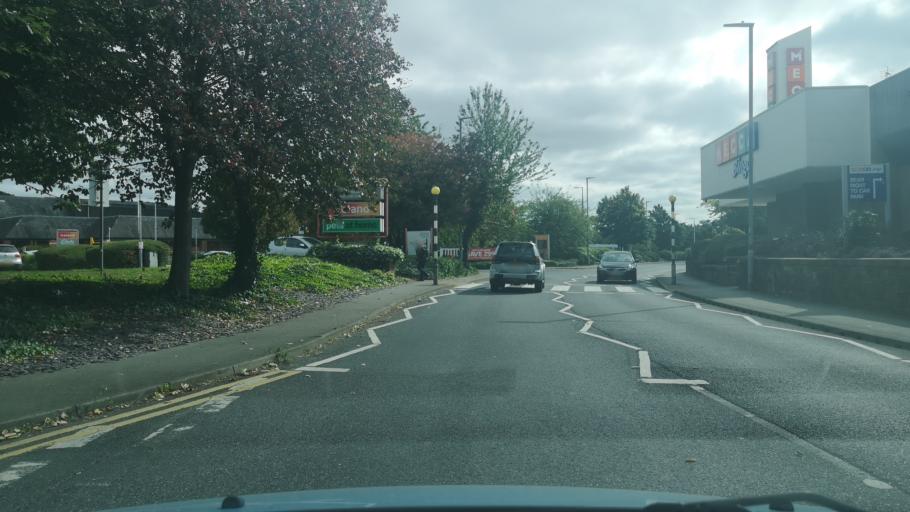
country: GB
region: England
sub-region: Kirklees
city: Dewsbury
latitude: 53.6902
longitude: -1.6256
